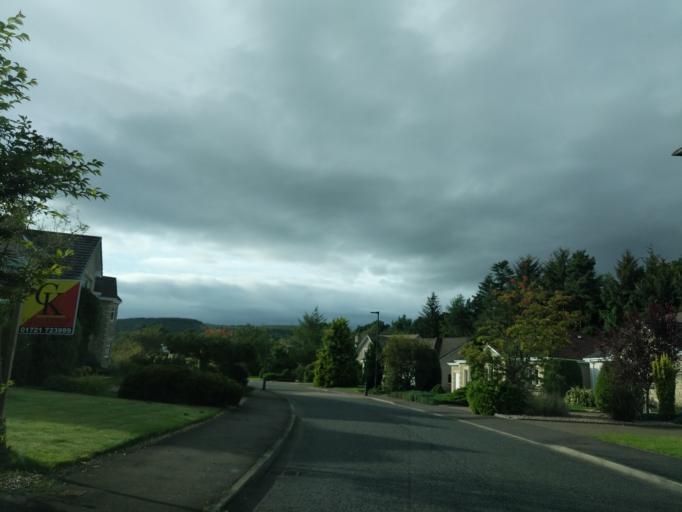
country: GB
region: Scotland
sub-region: The Scottish Borders
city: Innerleithen
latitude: 55.6392
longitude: -3.1039
